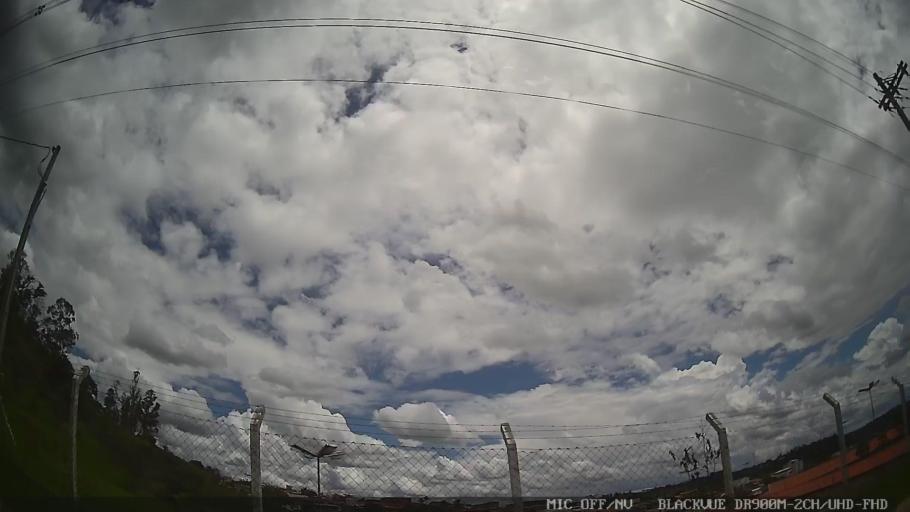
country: BR
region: Sao Paulo
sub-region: Jaguariuna
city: Jaguariuna
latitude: -22.7029
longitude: -46.9617
